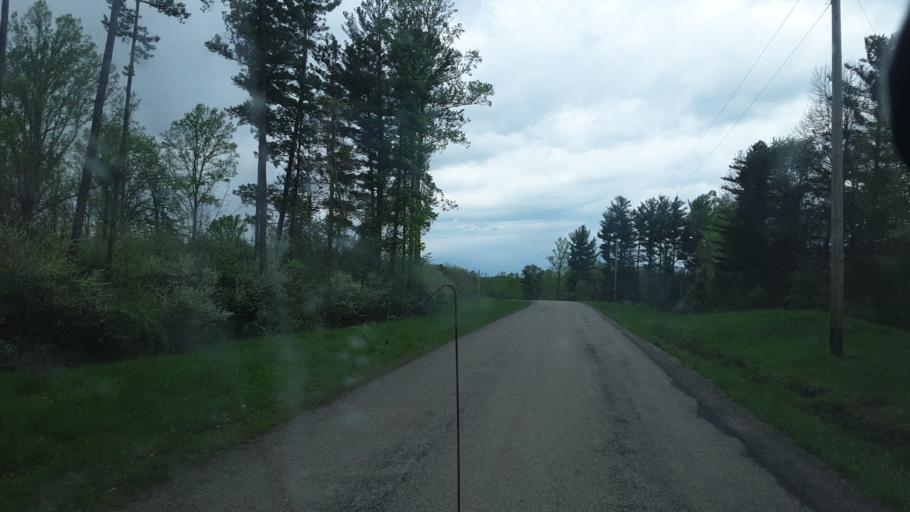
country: US
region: Ohio
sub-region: Noble County
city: Caldwell
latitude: 39.7291
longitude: -81.6795
